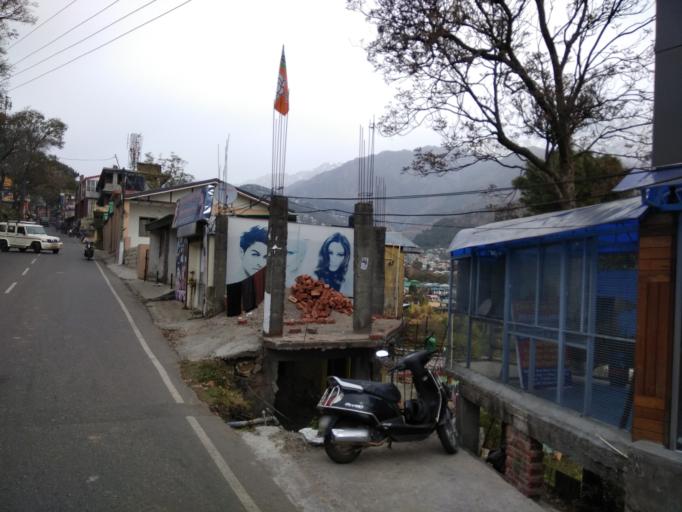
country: IN
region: Himachal Pradesh
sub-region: Kangra
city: Dharmsala
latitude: 32.2056
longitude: 76.3246
